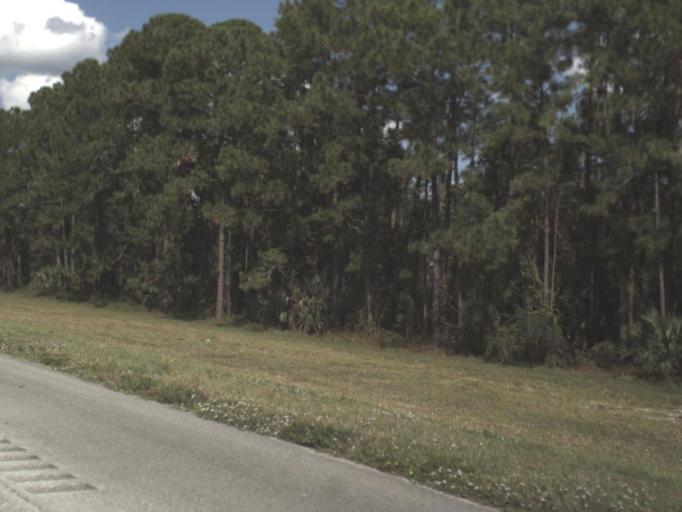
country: US
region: Florida
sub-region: Indian River County
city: Fellsmere
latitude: 27.5998
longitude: -80.8202
